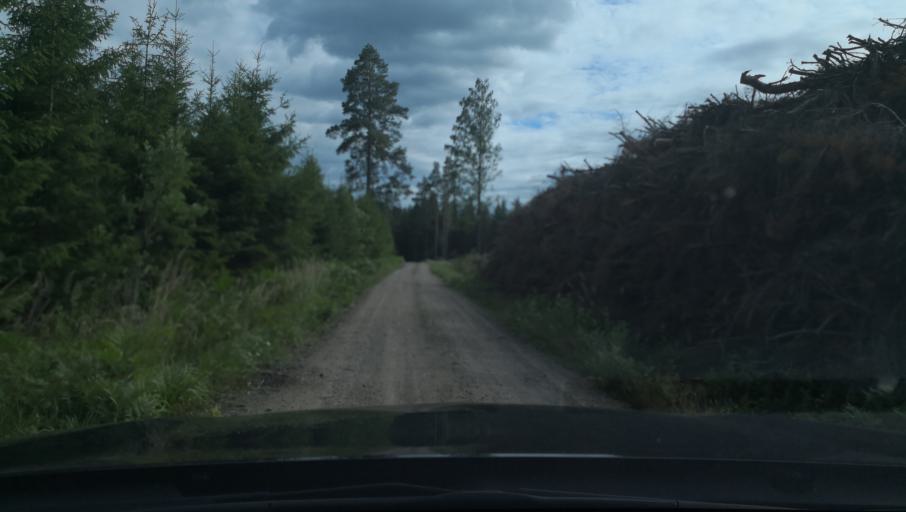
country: SE
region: Vaestmanland
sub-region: Hallstahammars Kommun
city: Hallstahammar
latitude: 59.6445
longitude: 16.0821
